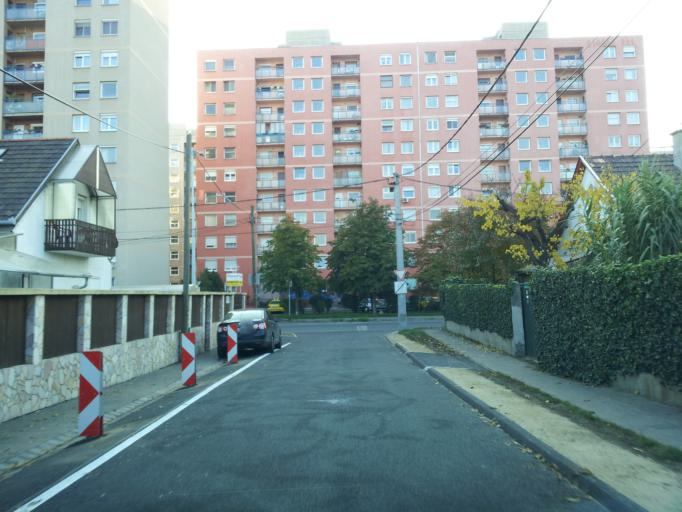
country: HU
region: Budapest
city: Budapest X. keruelet
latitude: 47.4738
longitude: 19.1646
